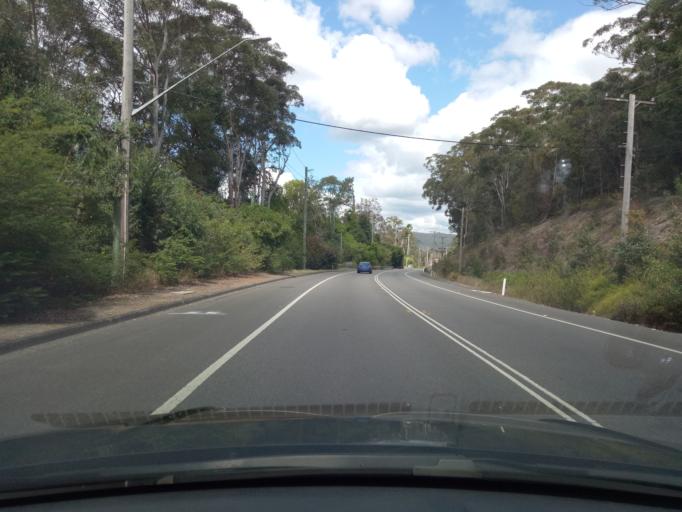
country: AU
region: New South Wales
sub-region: Gosford Shire
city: Gosford
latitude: -33.4102
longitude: 151.3357
